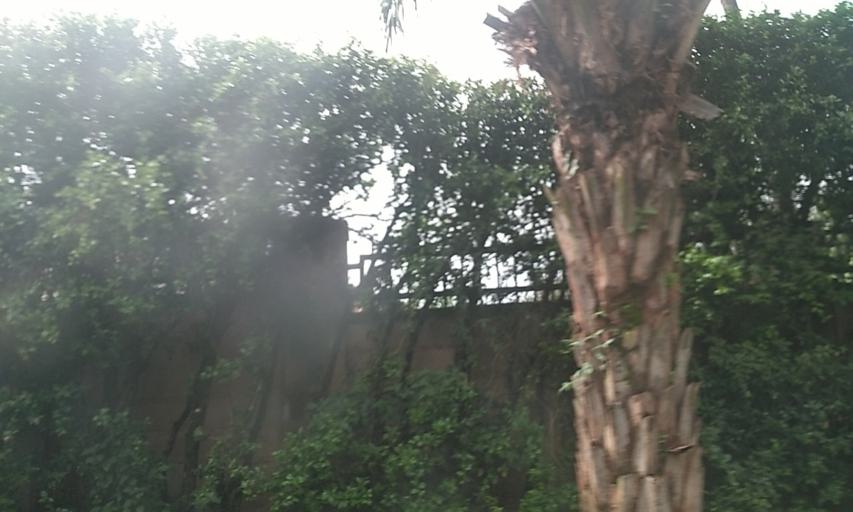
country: UG
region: Central Region
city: Kampala Central Division
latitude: 0.3299
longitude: 32.5883
